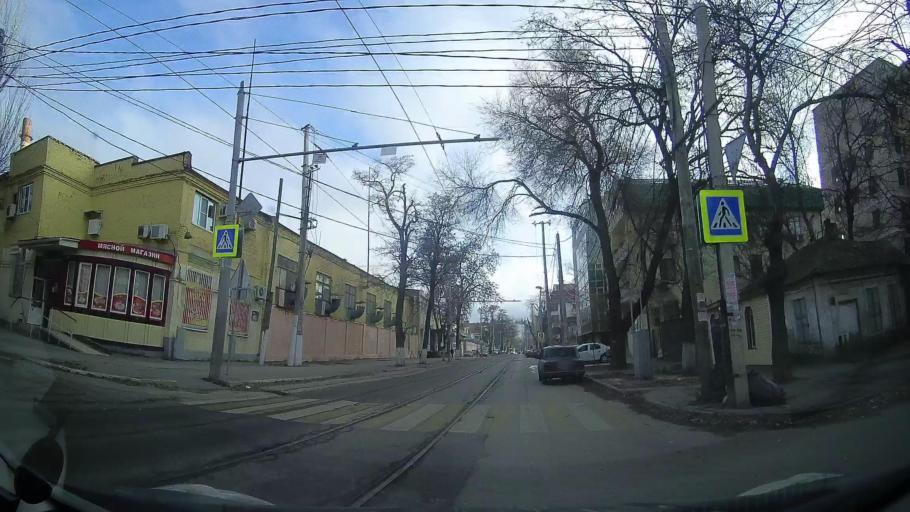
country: RU
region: Rostov
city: Rostov-na-Donu
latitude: 47.2349
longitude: 39.7329
